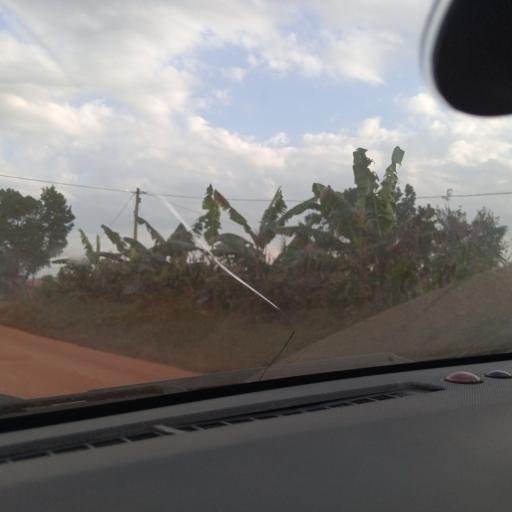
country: UG
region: Central Region
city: Masaka
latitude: -0.3322
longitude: 31.7042
